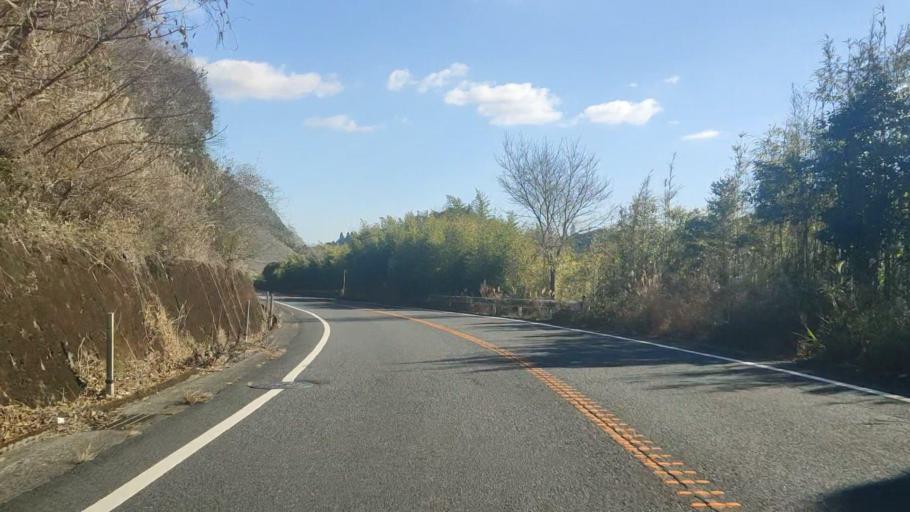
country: JP
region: Kagoshima
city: Sueyoshicho-ninokata
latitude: 31.6614
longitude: 130.8900
